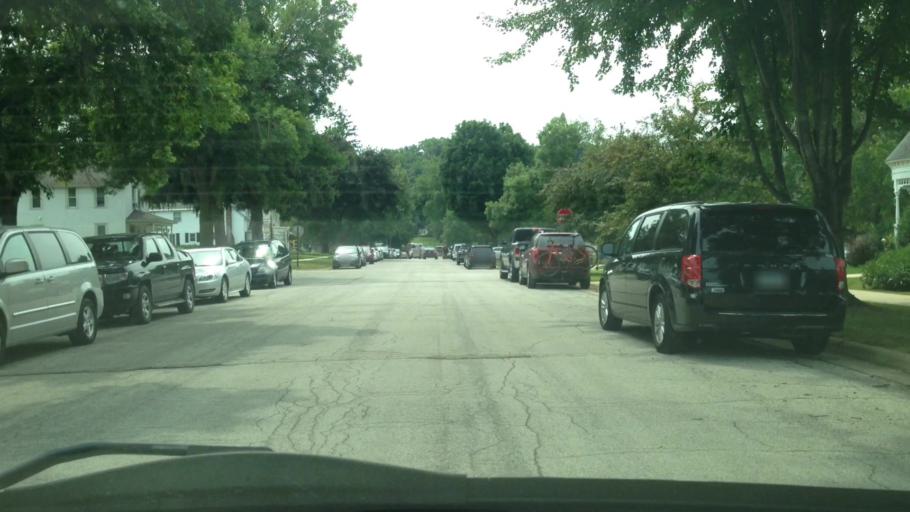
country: US
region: Minnesota
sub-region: Fillmore County
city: Preston
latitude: 43.7158
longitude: -91.9741
